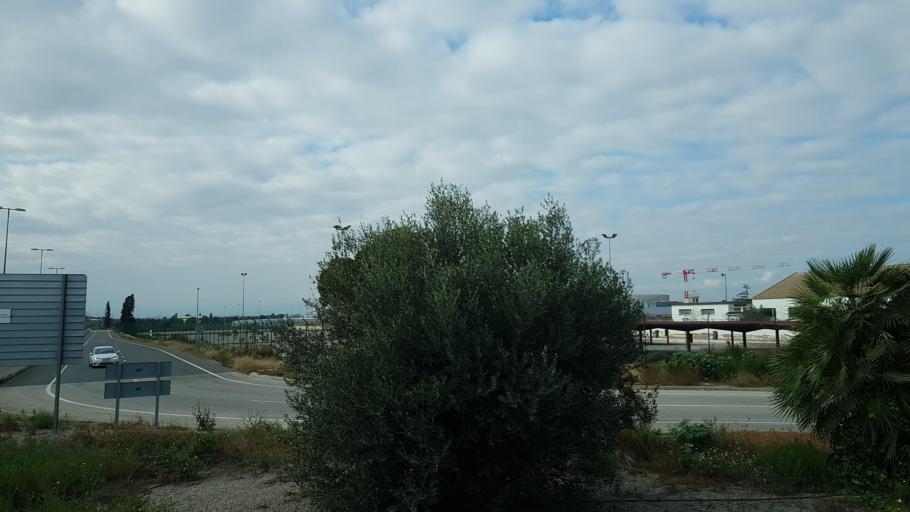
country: ES
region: Valencia
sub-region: Provincia de Valencia
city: Manises
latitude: 39.4767
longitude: -0.4837
